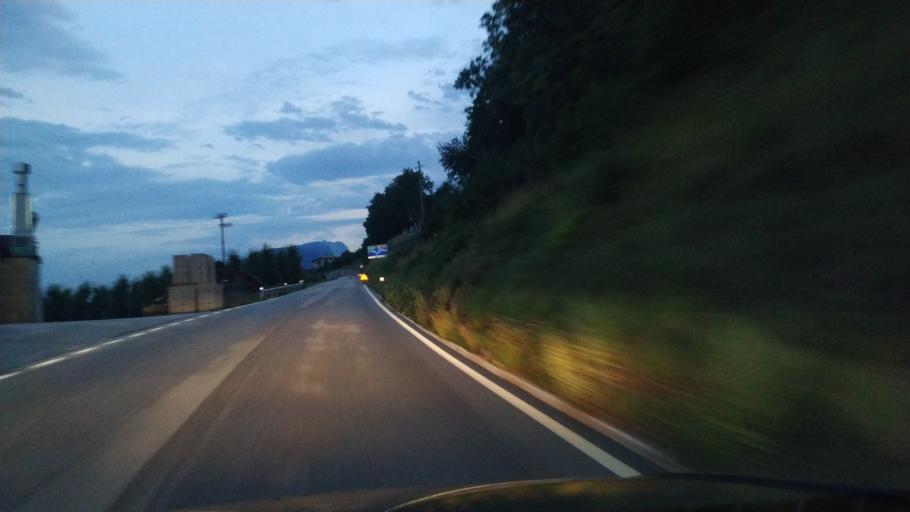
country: IT
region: Trentino-Alto Adige
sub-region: Provincia di Trento
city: Cles
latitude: 46.3787
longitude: 11.0358
